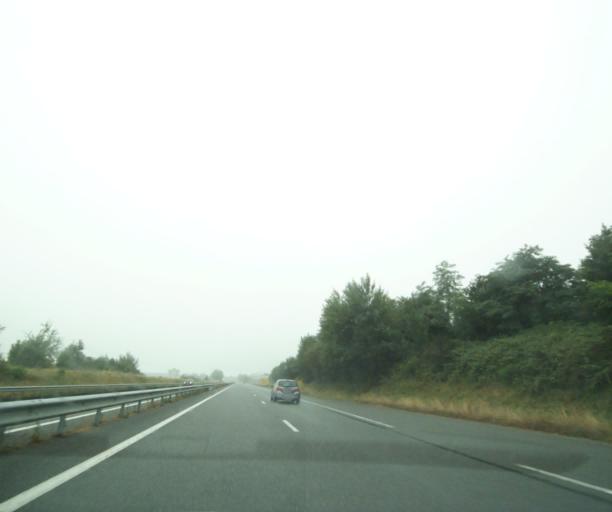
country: FR
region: Midi-Pyrenees
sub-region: Departement de l'Aveyron
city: Naucelle
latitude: 44.1348
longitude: 2.3101
